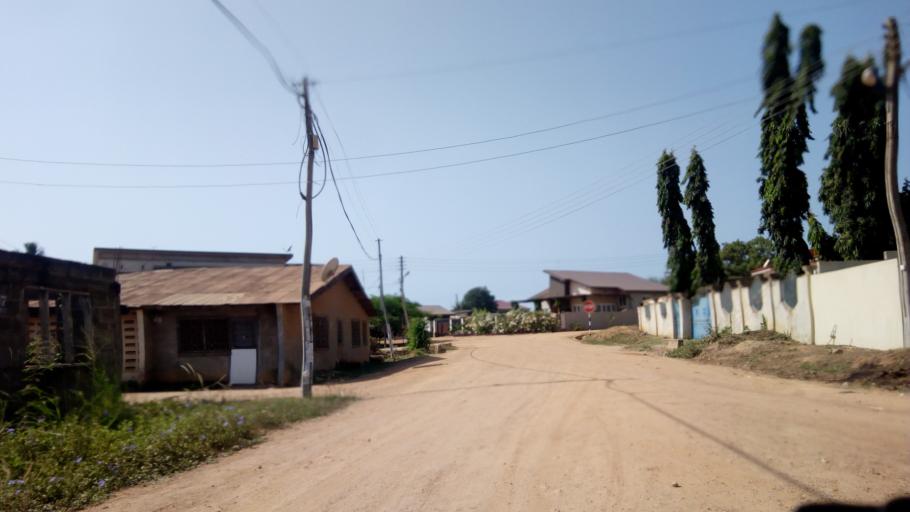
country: GH
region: Central
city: Cape Coast
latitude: 5.1190
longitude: -1.2705
